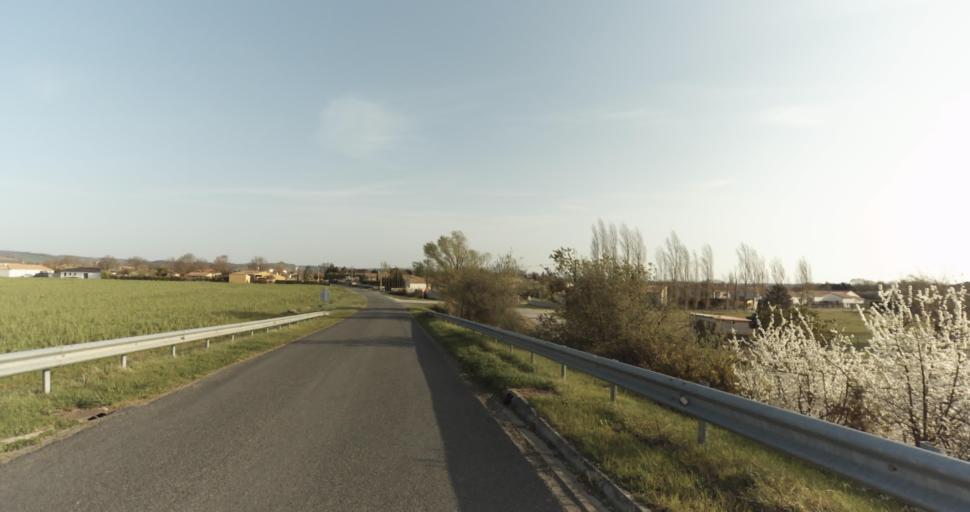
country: FR
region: Midi-Pyrenees
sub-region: Departement du Tarn
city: Saint-Sulpice-la-Pointe
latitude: 43.7548
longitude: 1.6873
